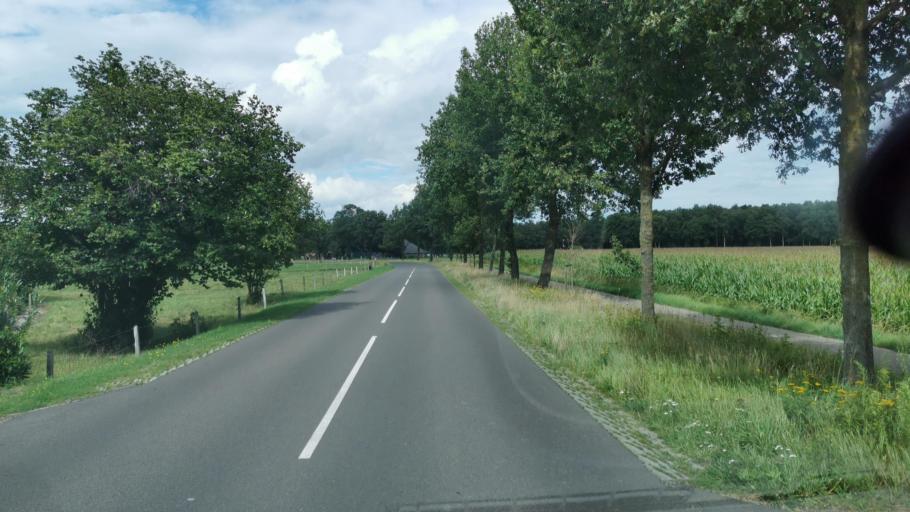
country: NL
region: Overijssel
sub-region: Gemeente Haaksbergen
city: Haaksbergen
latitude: 52.1481
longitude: 6.7959
